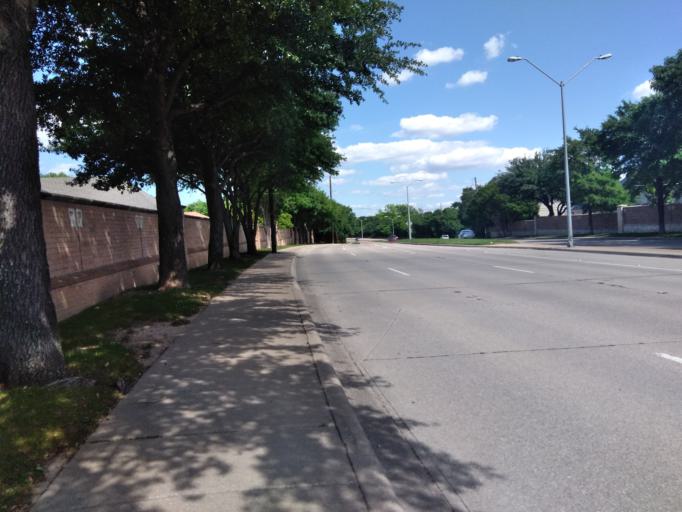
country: US
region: Texas
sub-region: Dallas County
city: Addison
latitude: 32.9992
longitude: -96.8169
